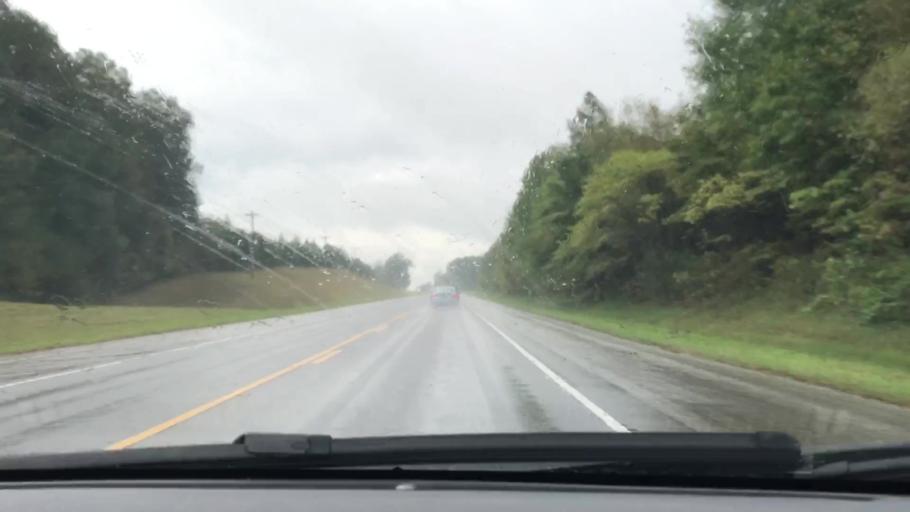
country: US
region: Tennessee
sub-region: Macon County
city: Lafayette
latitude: 36.5321
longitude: -86.0791
